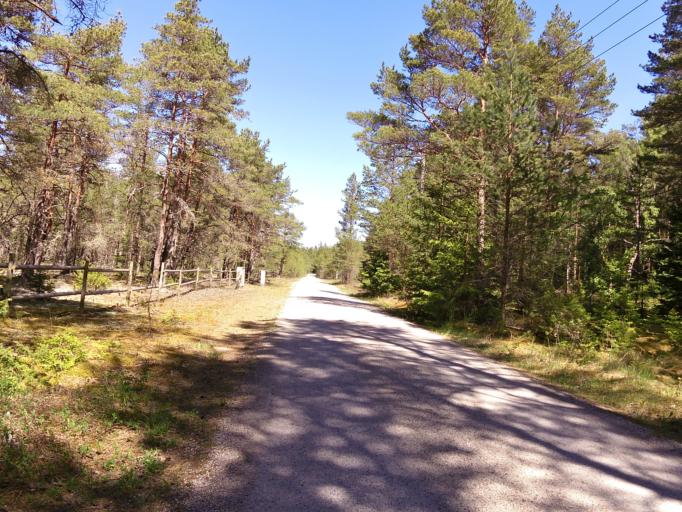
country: EE
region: Harju
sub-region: Paldiski linn
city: Paldiski
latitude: 59.2705
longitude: 23.7775
